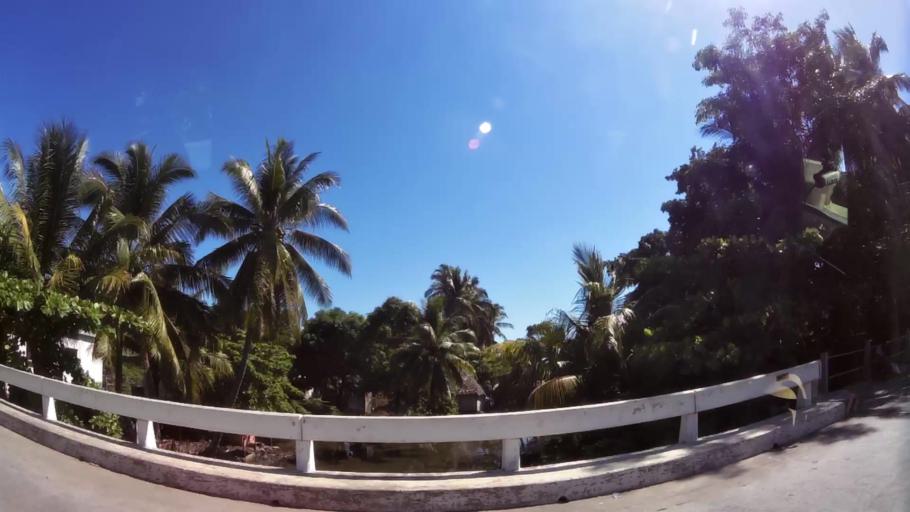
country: GT
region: Escuintla
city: Iztapa
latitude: 13.9369
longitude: -90.7144
